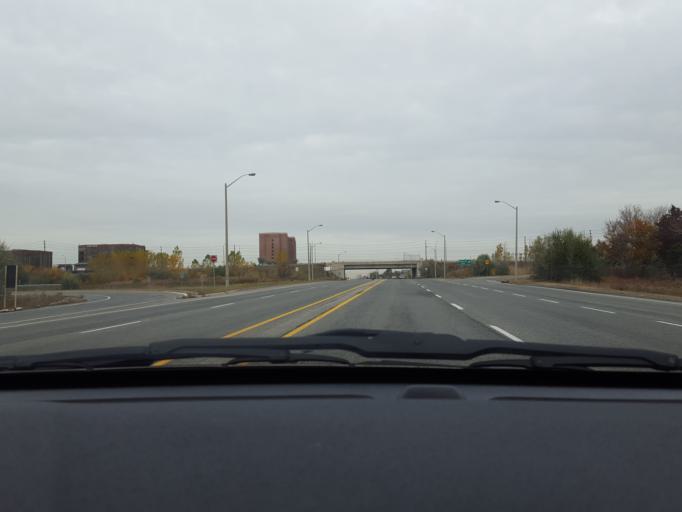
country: CA
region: Ontario
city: Etobicoke
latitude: 43.6862
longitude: -79.5811
